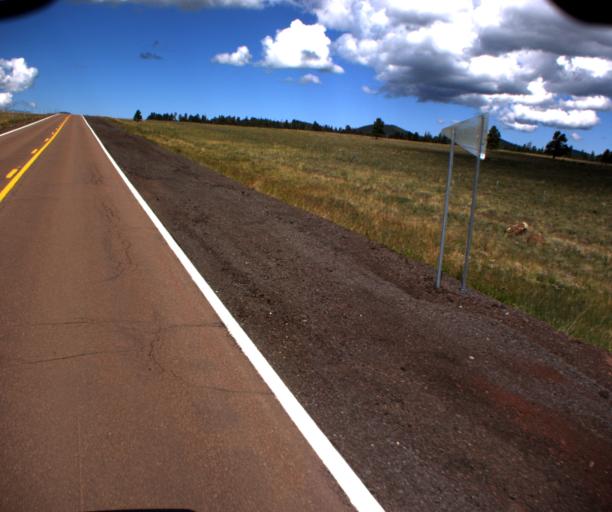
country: US
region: Arizona
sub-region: Apache County
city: Eagar
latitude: 34.0556
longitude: -109.5090
